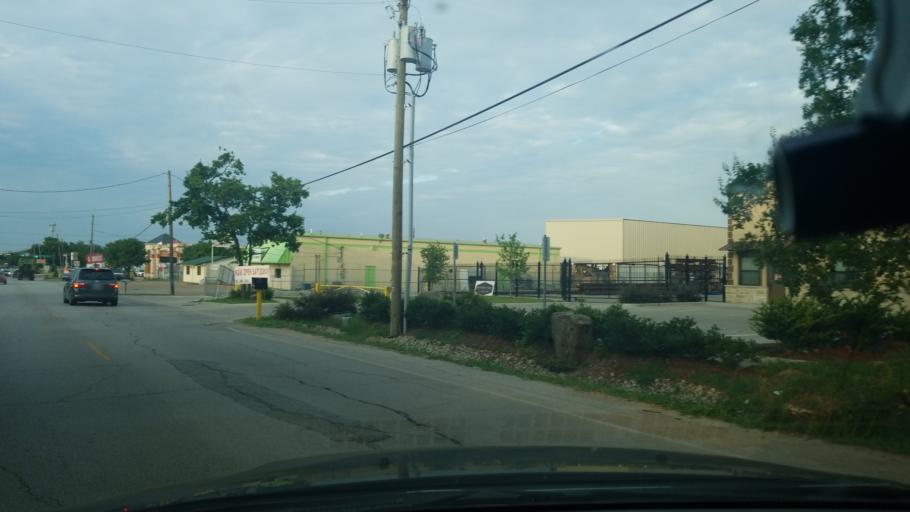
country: US
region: Texas
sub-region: Dallas County
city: Balch Springs
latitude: 32.7361
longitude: -96.6312
